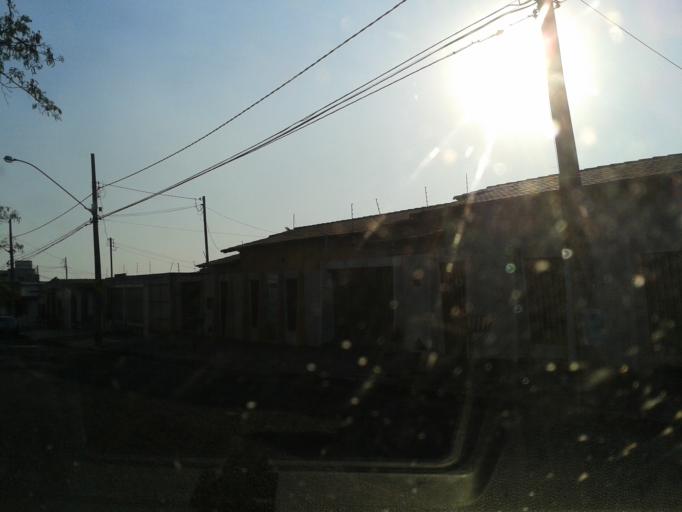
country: BR
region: Minas Gerais
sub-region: Uberlandia
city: Uberlandia
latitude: -18.8990
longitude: -48.2481
